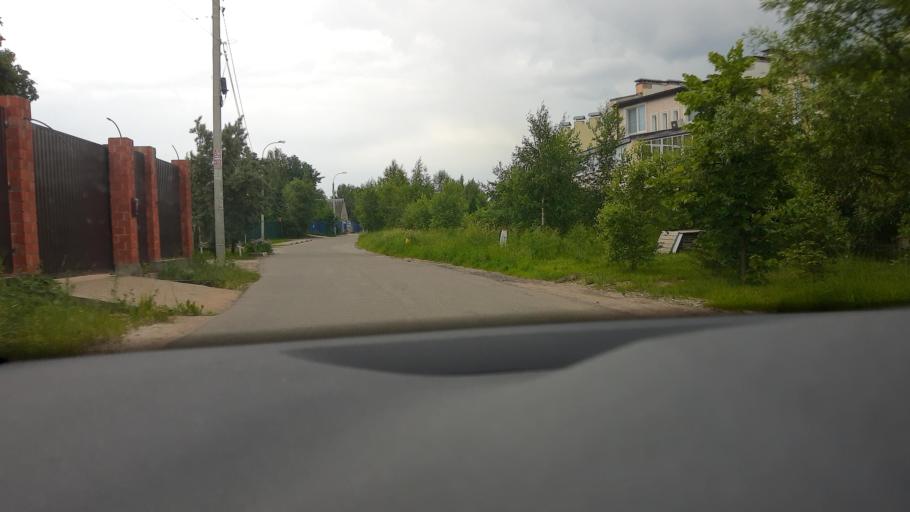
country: RU
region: Moscow
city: Khimki
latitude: 55.8794
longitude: 37.3689
